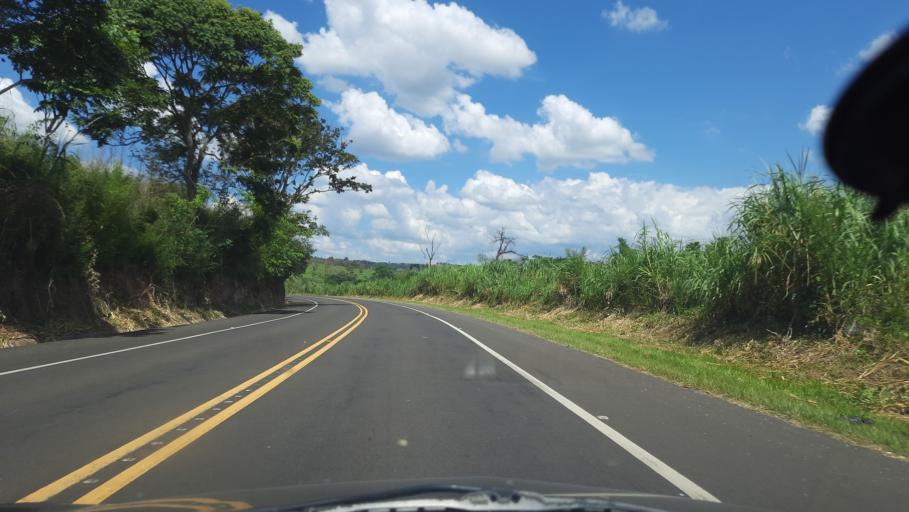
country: BR
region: Sao Paulo
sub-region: Sao Jose Do Rio Pardo
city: Sao Jose do Rio Pardo
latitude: -21.6047
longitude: -46.9723
